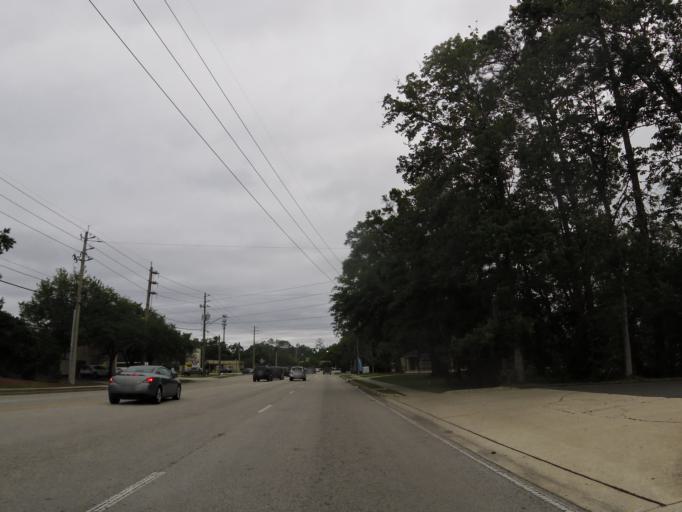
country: US
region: Florida
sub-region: Saint Johns County
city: Fruit Cove
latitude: 30.1825
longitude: -81.6071
